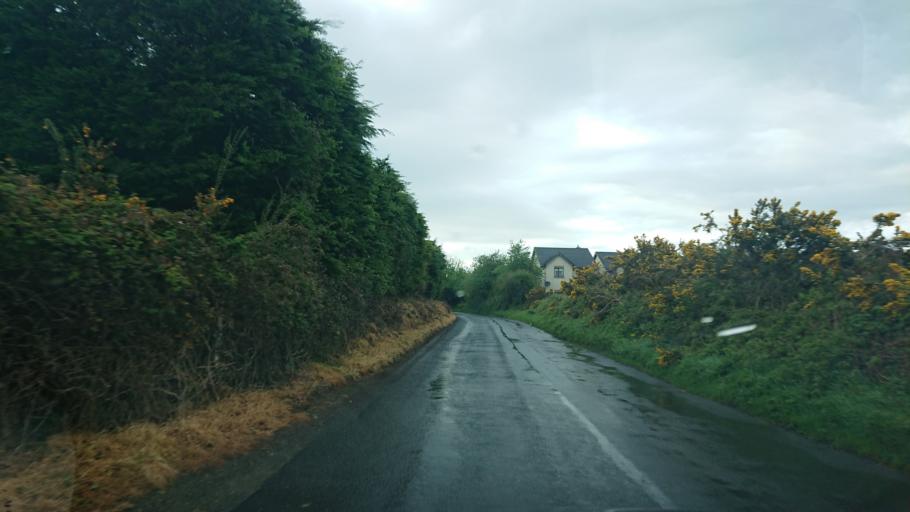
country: IE
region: Munster
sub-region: Waterford
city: Waterford
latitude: 52.2331
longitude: -7.0763
